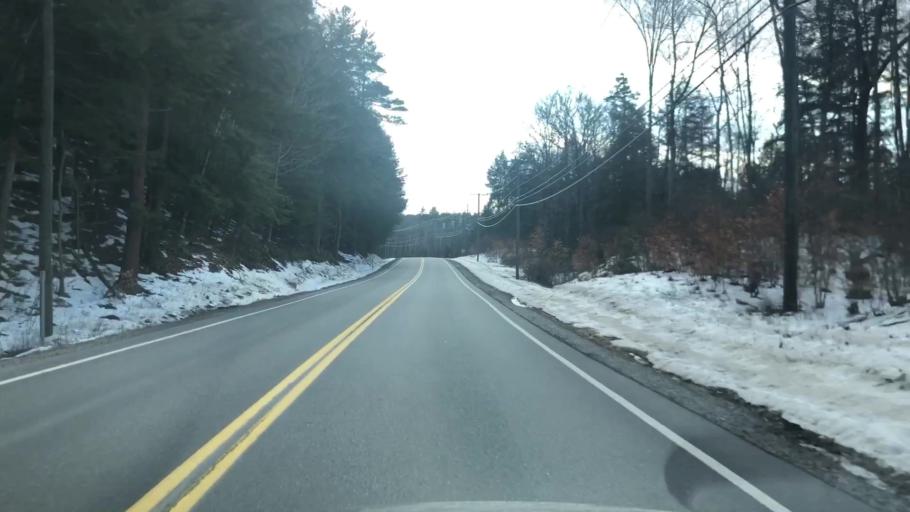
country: US
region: New Hampshire
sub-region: Hillsborough County
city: Mont Vernon
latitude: 42.8716
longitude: -71.6687
